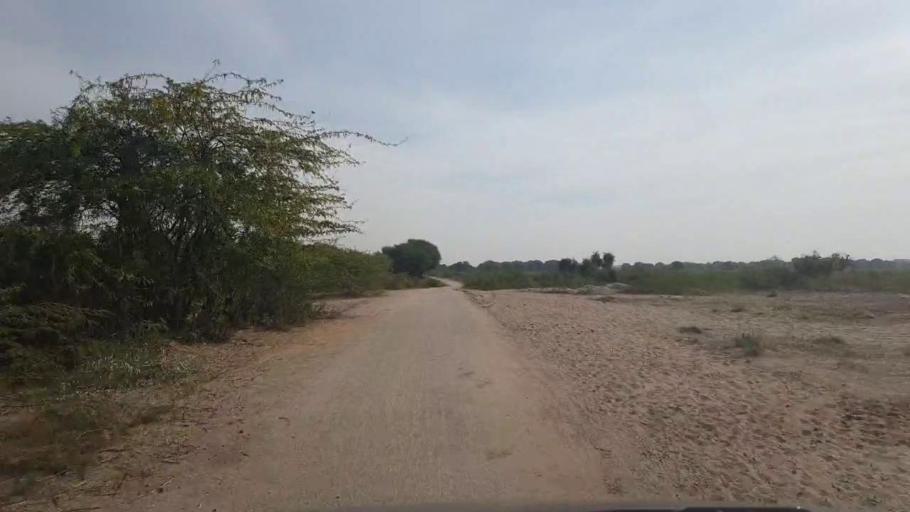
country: PK
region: Sindh
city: Umarkot
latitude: 25.2939
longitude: 69.7042
